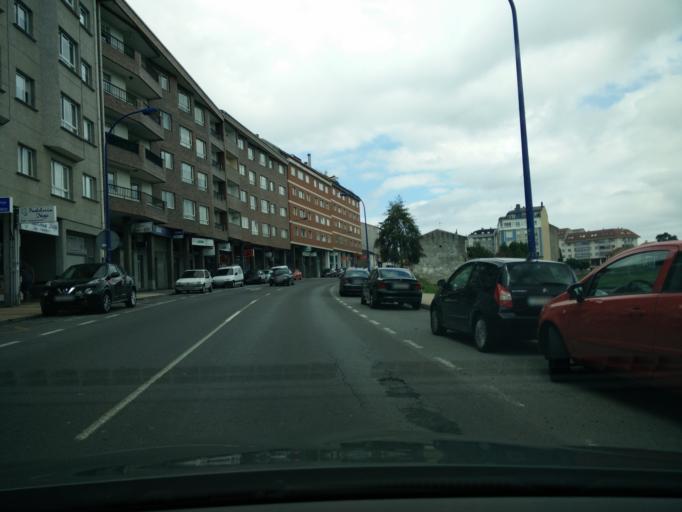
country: ES
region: Galicia
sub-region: Provincia da Coruna
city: Culleredo
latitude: 43.3187
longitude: -8.3843
